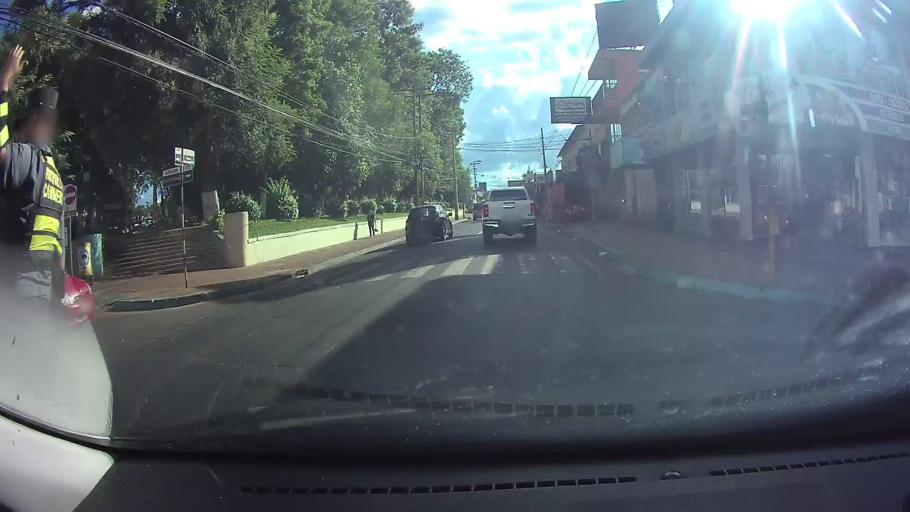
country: PY
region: Cordillera
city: Caacupe
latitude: -25.3854
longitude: -57.1422
